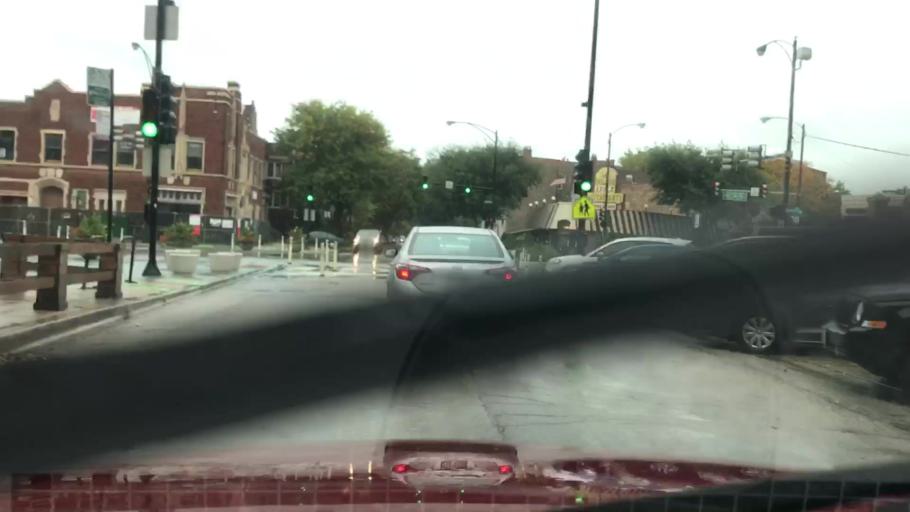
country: US
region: Illinois
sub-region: Cook County
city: Chicago
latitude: 41.9361
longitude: -87.6643
